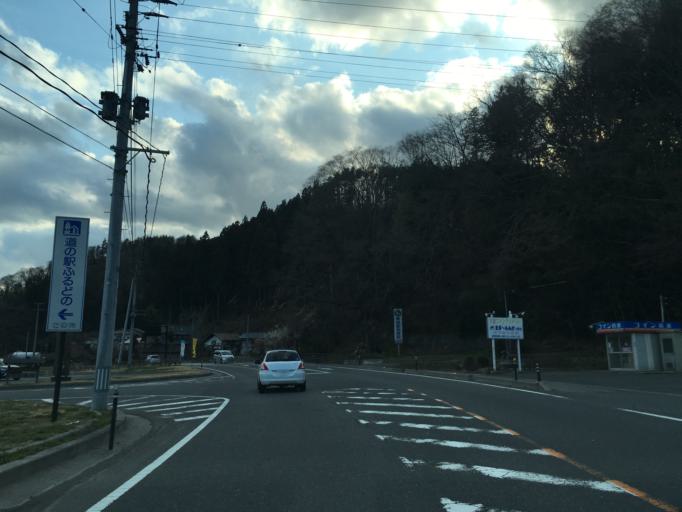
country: JP
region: Fukushima
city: Ishikawa
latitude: 37.0934
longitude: 140.5296
